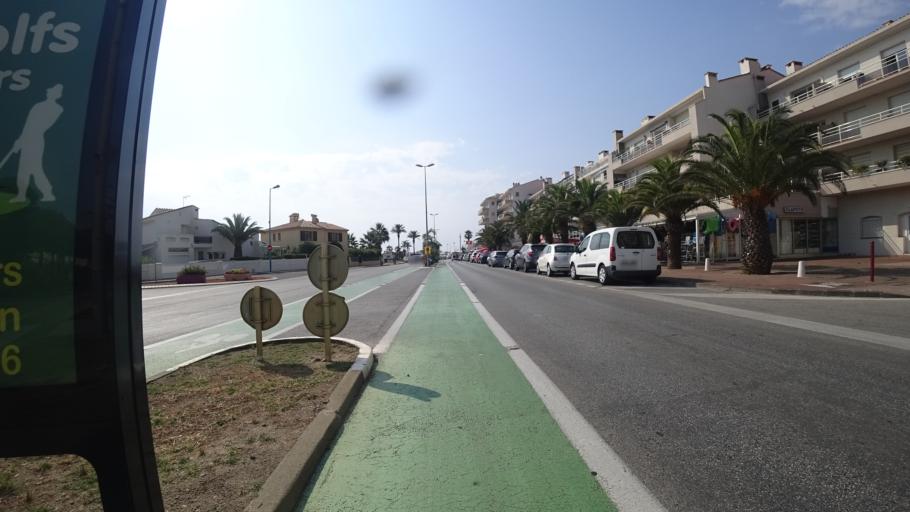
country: FR
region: Languedoc-Roussillon
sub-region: Departement des Pyrenees-Orientales
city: Saint-Cyprien-Plage
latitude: 42.6243
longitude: 3.0356
